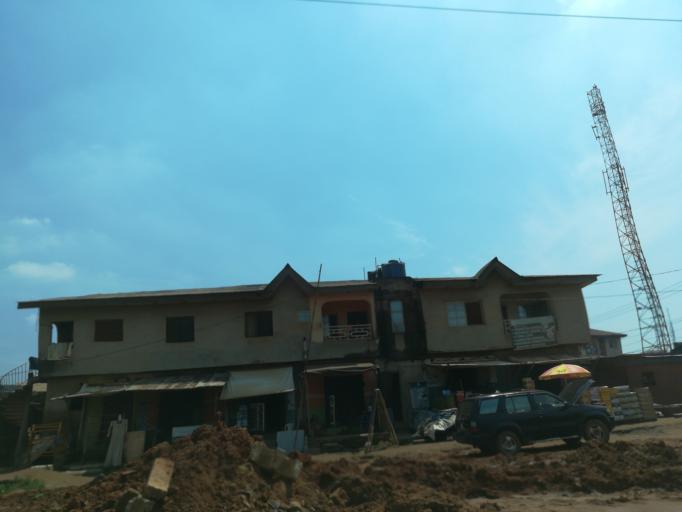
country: NG
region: Lagos
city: Ikorodu
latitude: 6.6483
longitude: 3.4777
